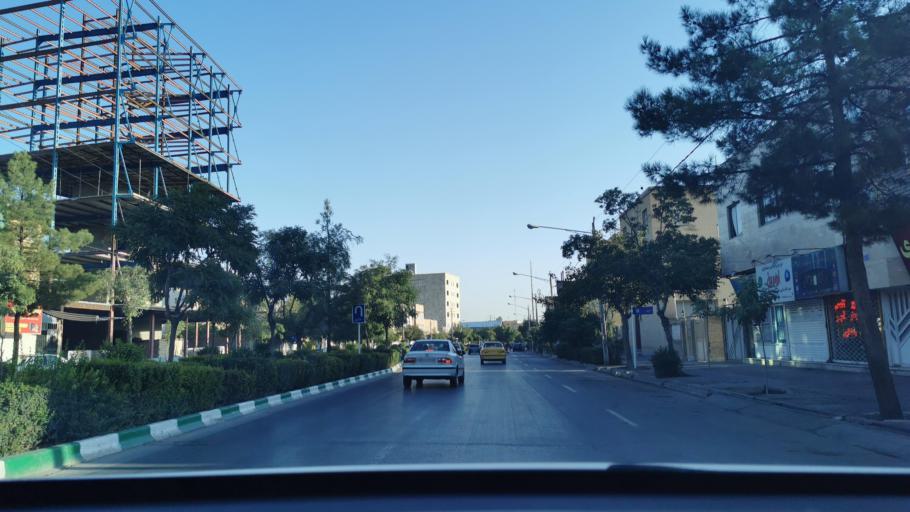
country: IR
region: Razavi Khorasan
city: Mashhad
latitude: 36.3540
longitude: 59.5132
